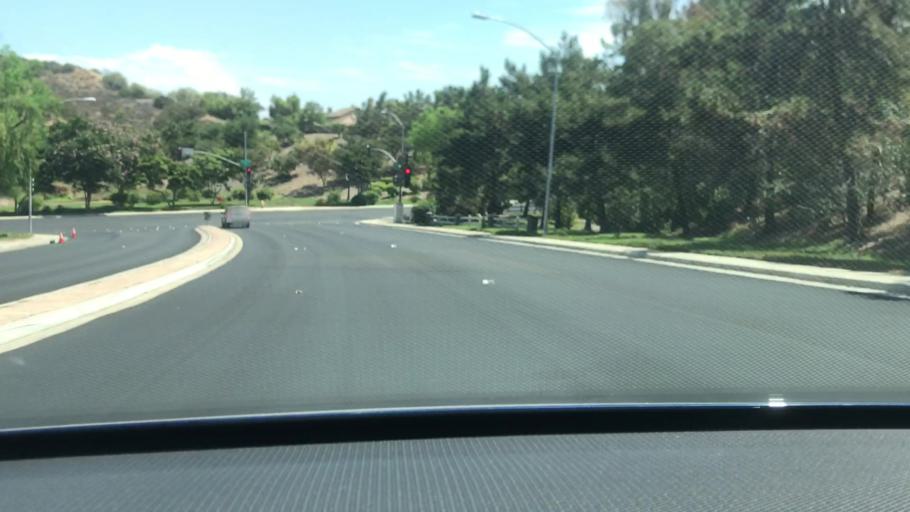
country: US
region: California
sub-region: San Diego County
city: Poway
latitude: 32.9254
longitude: -117.0934
